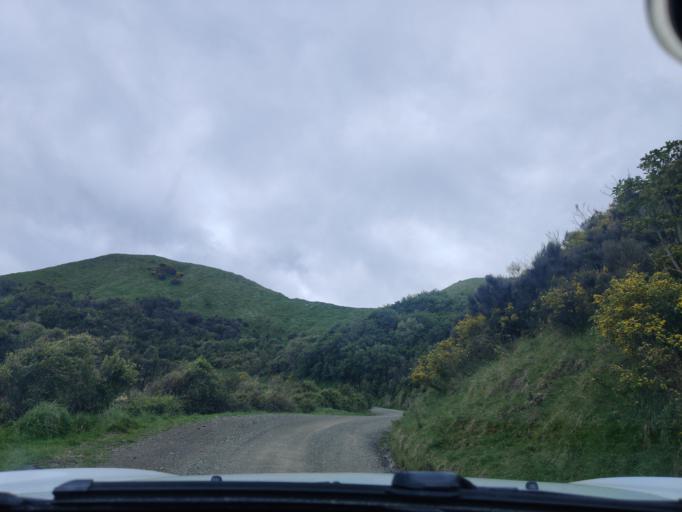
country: NZ
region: Manawatu-Wanganui
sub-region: Palmerston North City
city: Palmerston North
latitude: -40.2897
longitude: 175.8611
